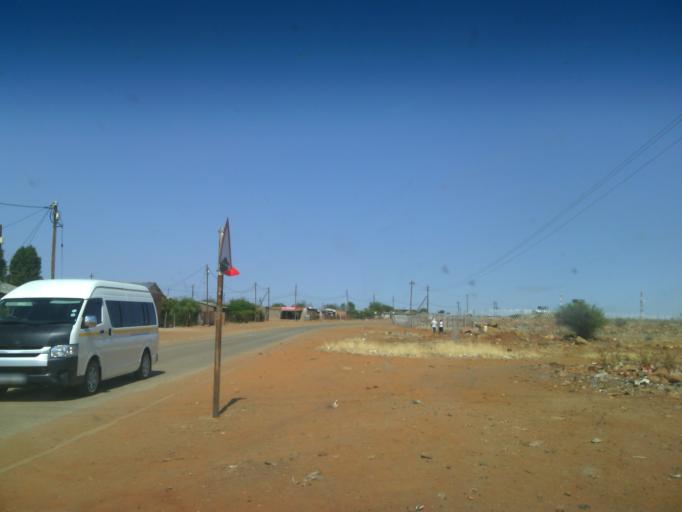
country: ZA
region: Northern Cape
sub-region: Frances Baard District Municipality
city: Barkly West
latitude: -28.5207
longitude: 24.5039
